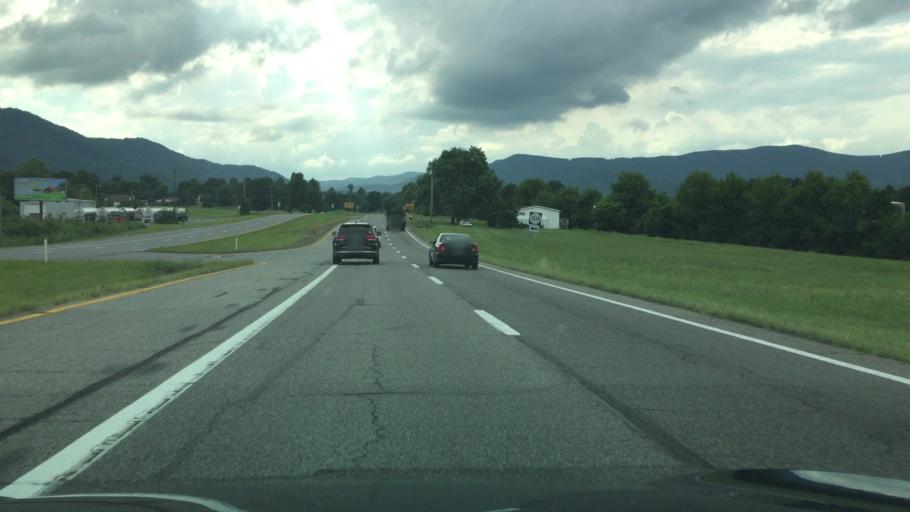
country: US
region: Virginia
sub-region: Botetourt County
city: Blue Ridge
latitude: 37.3779
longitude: -79.7127
